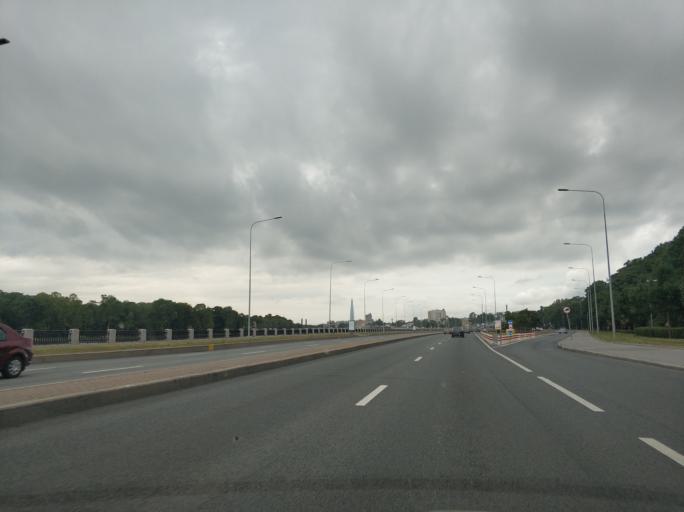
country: RU
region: Leningrad
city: Chernaya Rechka
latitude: 59.9821
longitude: 30.3102
